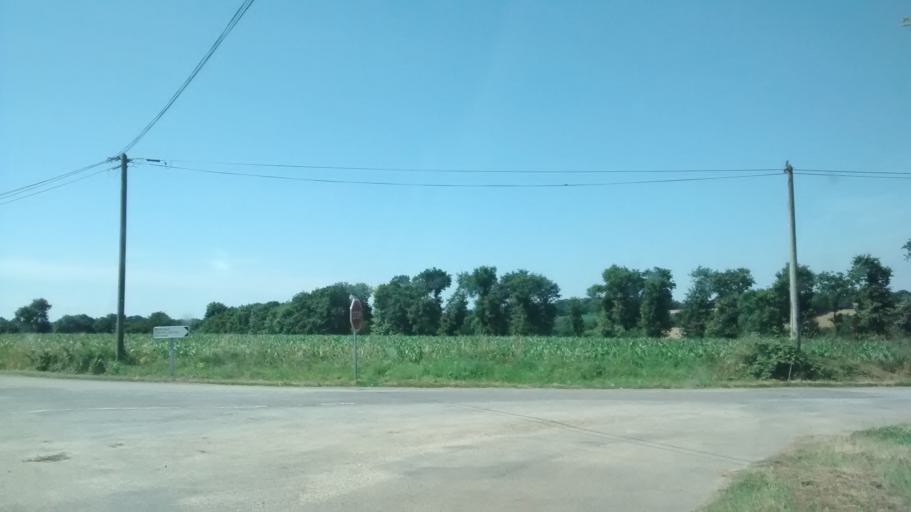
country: FR
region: Brittany
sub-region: Departement du Morbihan
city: Campeneac
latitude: 47.9721
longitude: -2.3061
